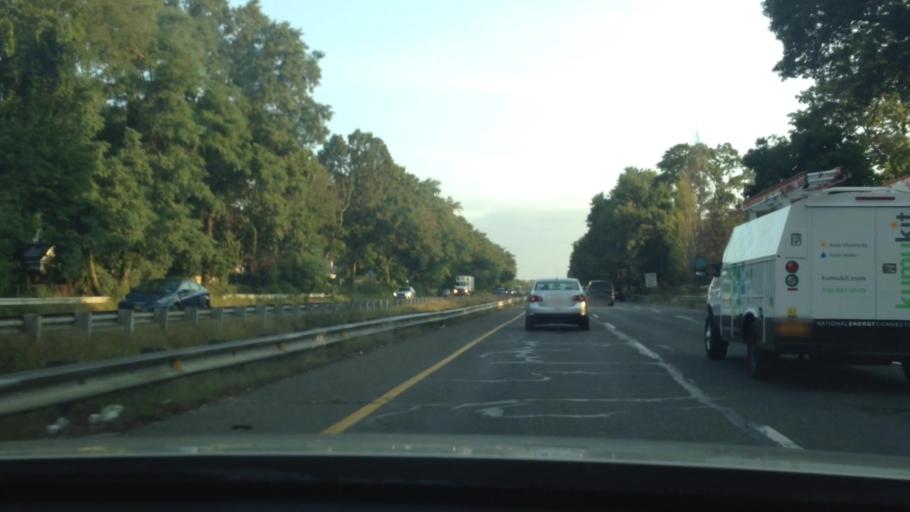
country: US
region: New York
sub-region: Suffolk County
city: Farmingville
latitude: 40.8368
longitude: -73.0210
